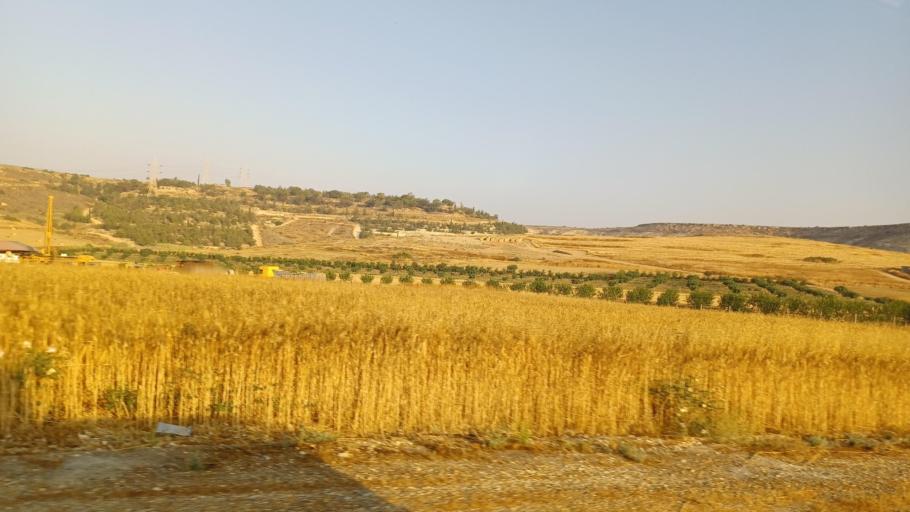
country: CY
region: Larnaka
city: Pyla
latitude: 35.0060
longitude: 33.6832
